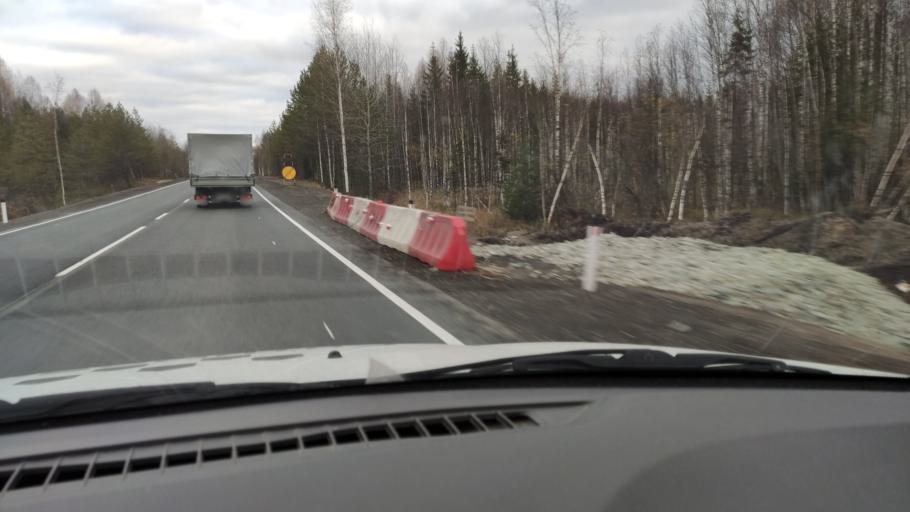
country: RU
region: Kirov
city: Chernaya Kholunitsa
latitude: 58.8745
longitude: 51.4949
